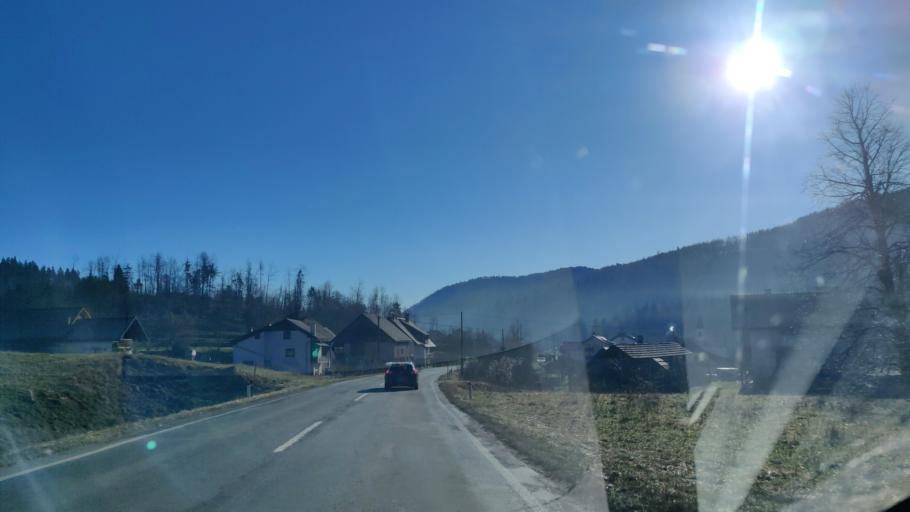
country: SI
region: Logatec
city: Logatec
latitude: 45.8761
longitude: 14.2110
